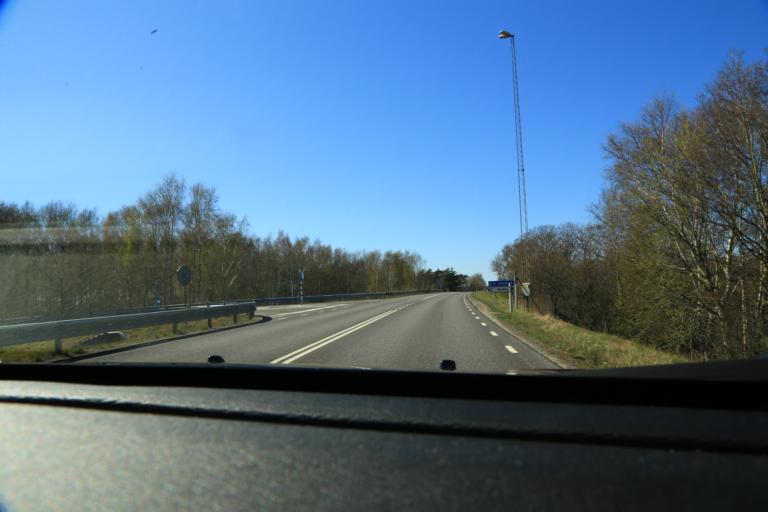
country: SE
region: Halland
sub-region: Varbergs Kommun
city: Traslovslage
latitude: 57.0495
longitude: 12.3098
